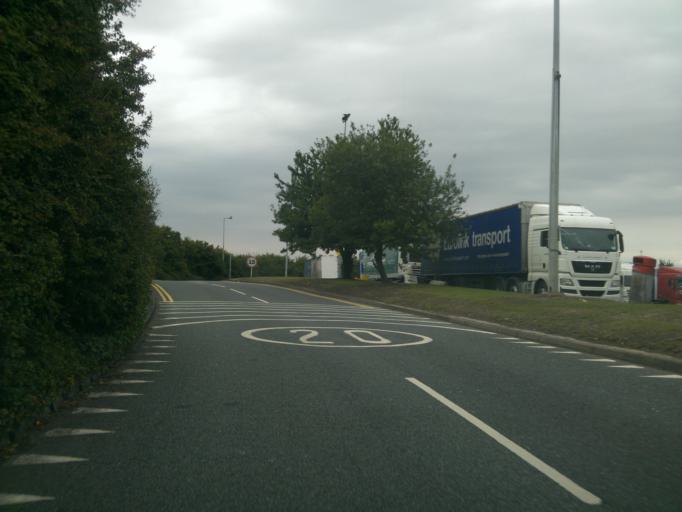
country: GB
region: England
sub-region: Kent
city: West Thurrock
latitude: 51.4907
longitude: 0.2706
